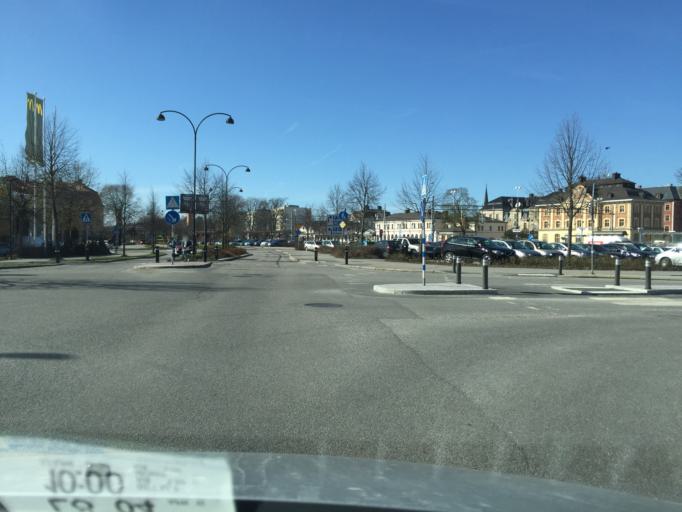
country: SE
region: Soedermanland
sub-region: Katrineholms Kommun
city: Katrineholm
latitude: 58.9955
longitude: 16.2110
